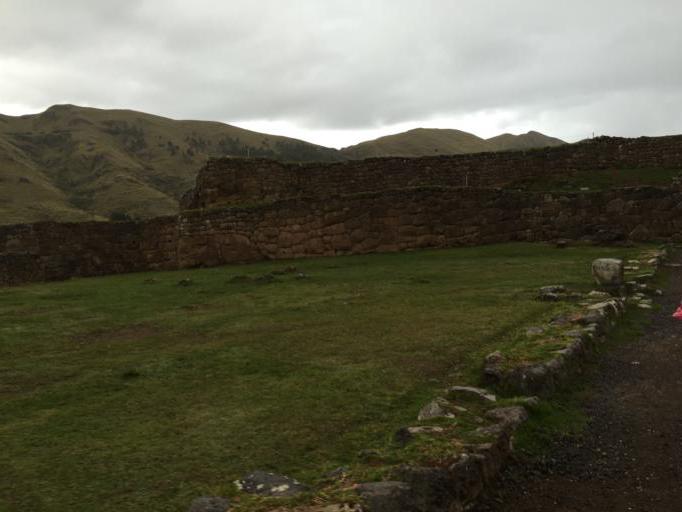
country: PE
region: Cusco
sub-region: Provincia de Cusco
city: Cusco
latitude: -13.4835
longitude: -71.9624
